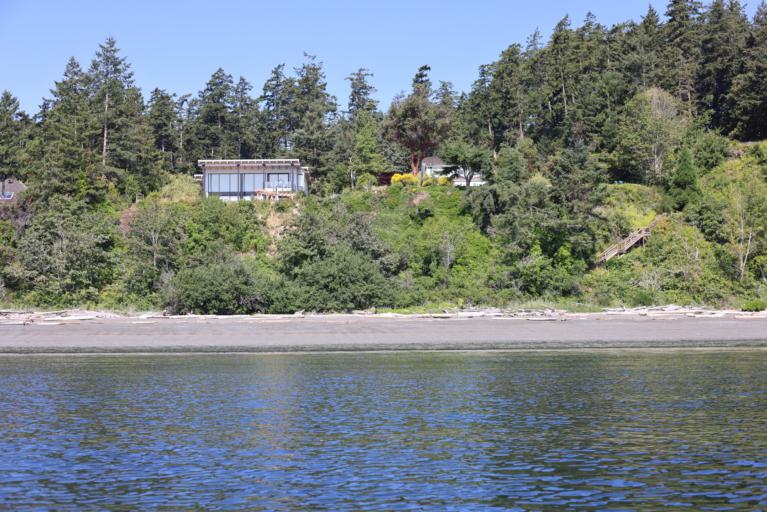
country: CA
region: British Columbia
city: Colwood
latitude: 48.3984
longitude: -123.4852
